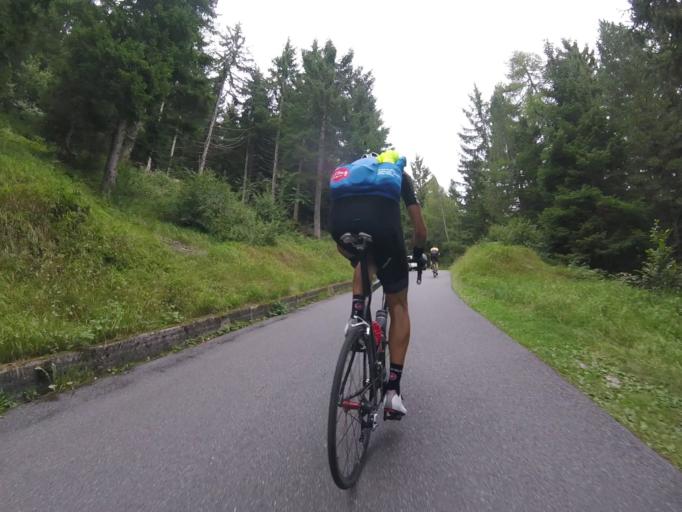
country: IT
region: Lombardy
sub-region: Provincia di Sondrio
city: Mazzo di Valtellina
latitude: 46.2546
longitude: 10.2898
